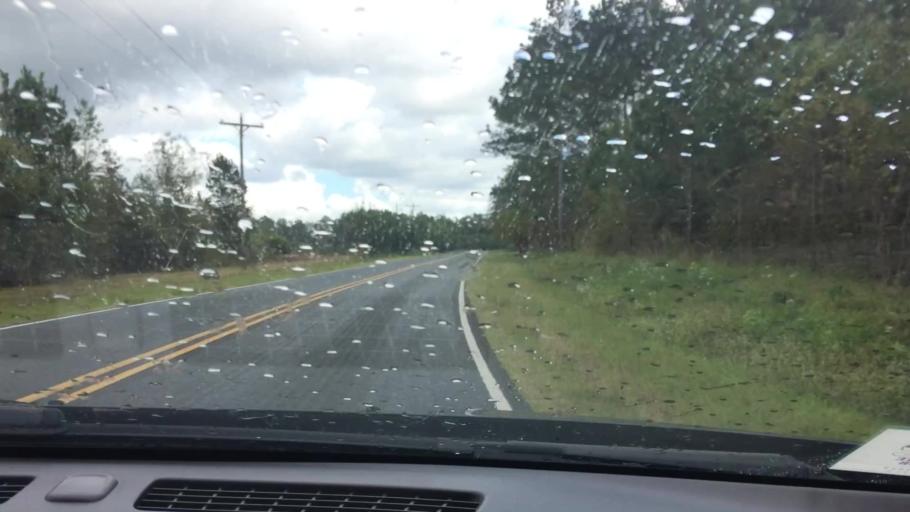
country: US
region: North Carolina
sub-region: Greene County
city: Maury
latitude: 35.5207
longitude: -77.5373
